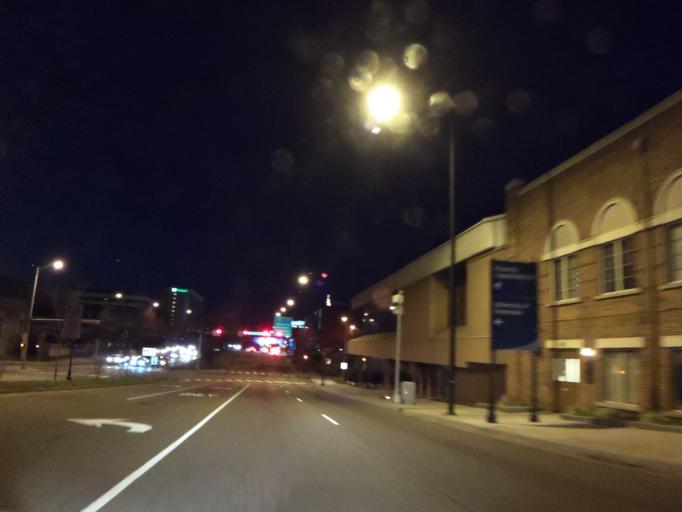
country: US
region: Tennessee
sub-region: Knox County
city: Knoxville
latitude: 35.9603
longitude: -83.9205
